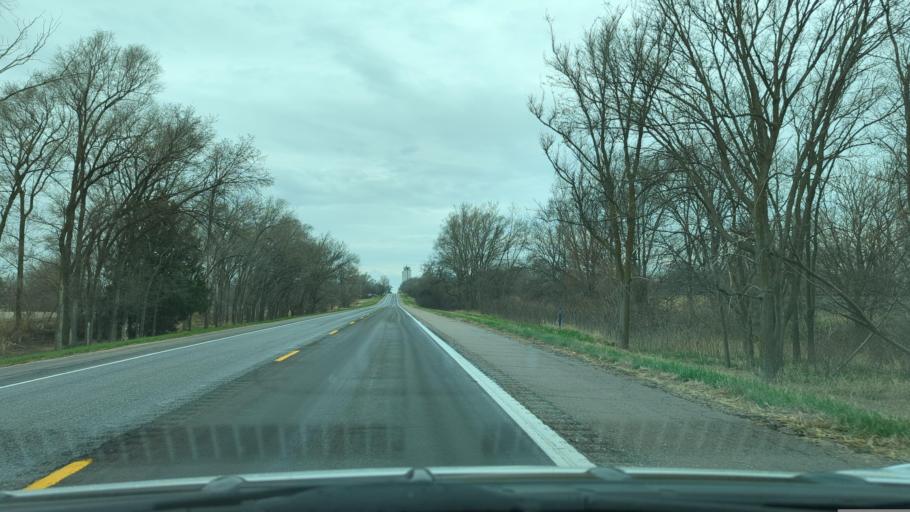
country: US
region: Nebraska
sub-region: Saunders County
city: Ashland
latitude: 40.9715
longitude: -96.4323
